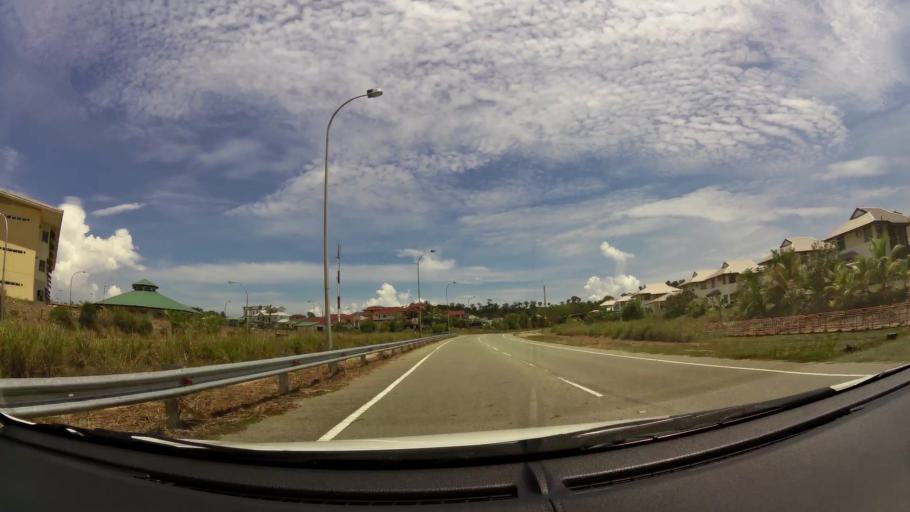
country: BN
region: Brunei and Muara
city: Bandar Seri Begawan
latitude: 4.9655
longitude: 114.9040
